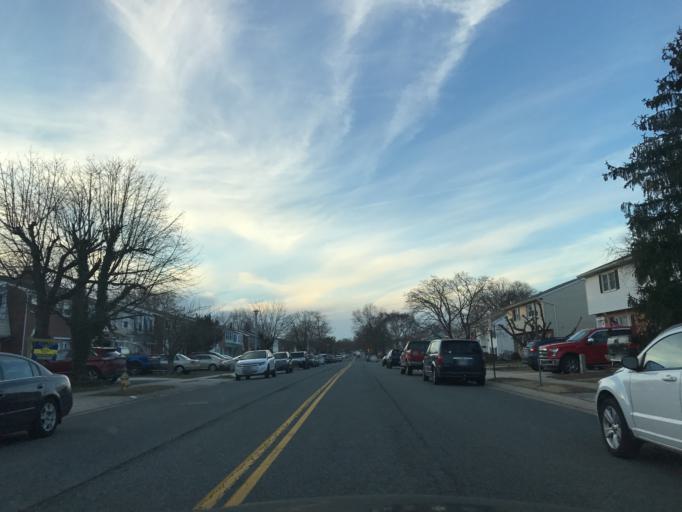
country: US
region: Maryland
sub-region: Harford County
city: Joppatowne
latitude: 39.4078
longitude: -76.3593
